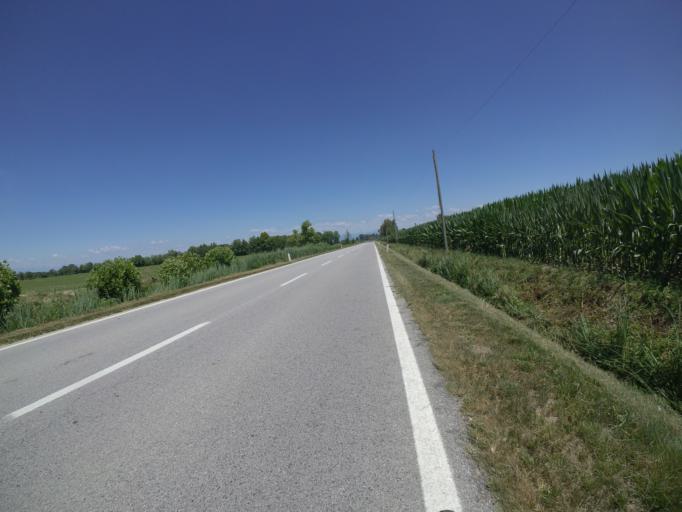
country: IT
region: Friuli Venezia Giulia
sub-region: Provincia di Udine
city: Rivignano
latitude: 45.8923
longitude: 13.0796
